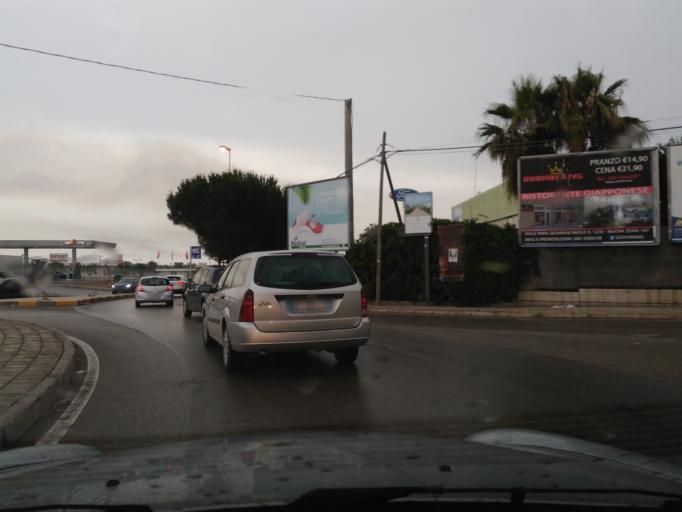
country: IT
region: Apulia
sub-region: Provincia di Bari
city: Molfetta
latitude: 41.2046
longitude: 16.5591
